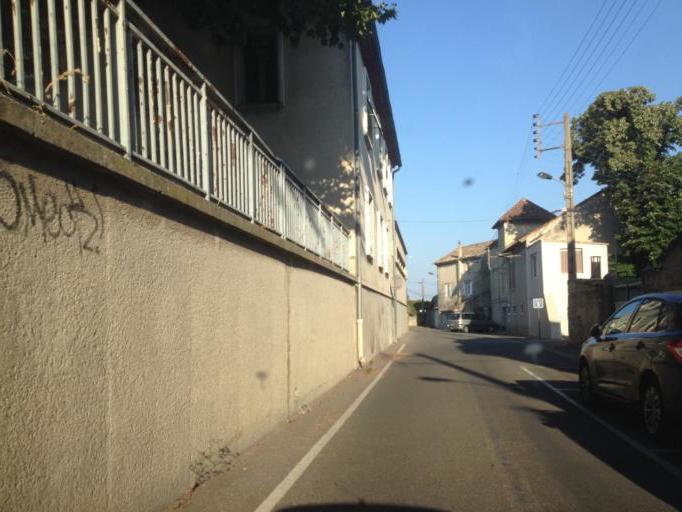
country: FR
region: Provence-Alpes-Cote d'Azur
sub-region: Departement du Vaucluse
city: Orange
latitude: 44.1370
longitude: 4.8196
